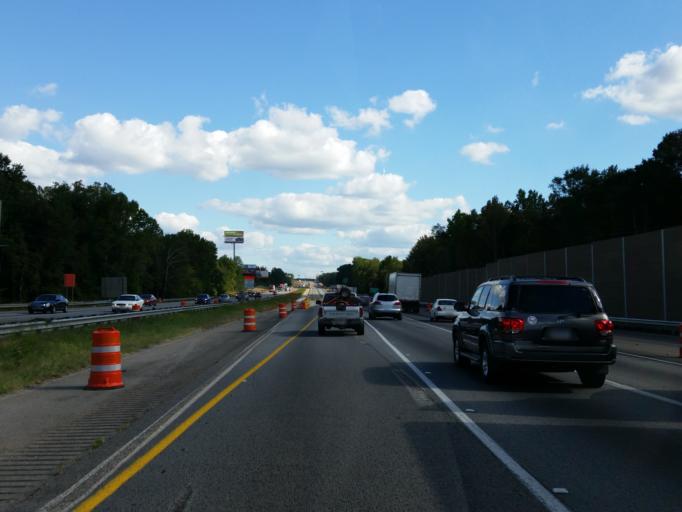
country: US
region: Georgia
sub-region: Henry County
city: McDonough
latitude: 33.4476
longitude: -84.2001
